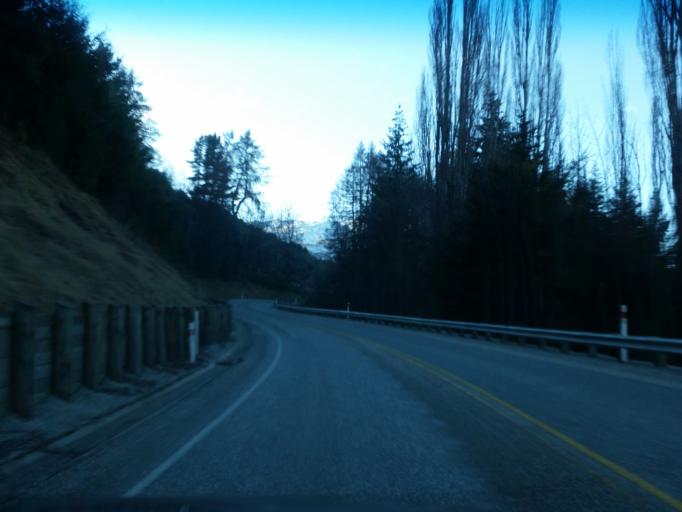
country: NZ
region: Otago
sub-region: Queenstown-Lakes District
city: Queenstown
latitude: -44.9723
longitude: 168.6971
